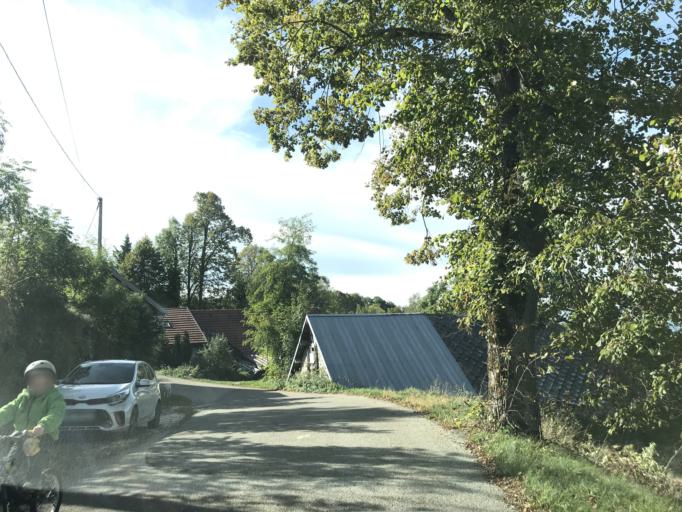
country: FR
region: Rhone-Alpes
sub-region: Departement de la Savoie
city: Novalaise
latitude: 45.6327
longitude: 5.8004
